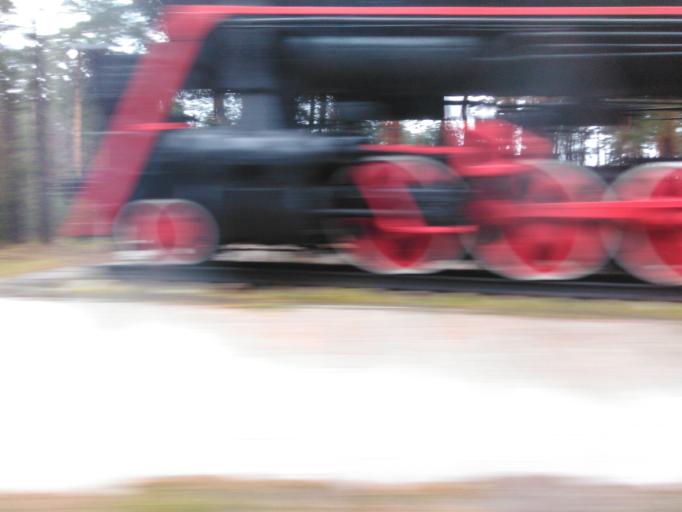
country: RU
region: Tatarstan
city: Osinovo
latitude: 55.8262
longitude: 48.8969
